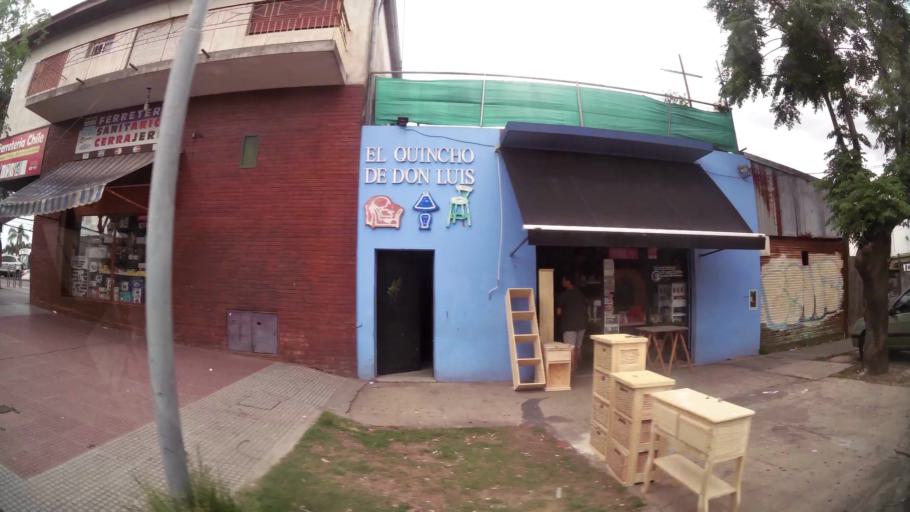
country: AR
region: Buenos Aires
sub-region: Partido de Tigre
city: Tigre
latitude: -34.4684
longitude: -58.6488
